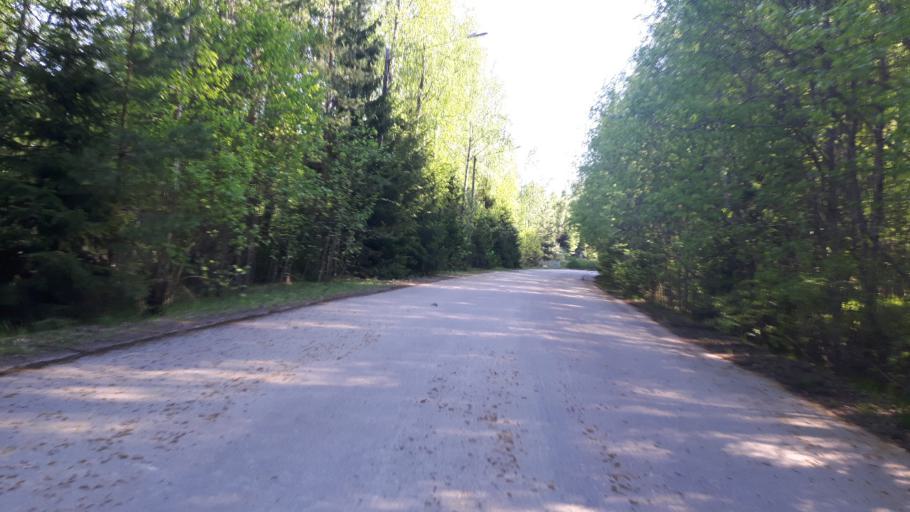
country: FI
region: Kymenlaakso
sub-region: Kotka-Hamina
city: Kotka
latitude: 60.4500
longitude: 26.8952
